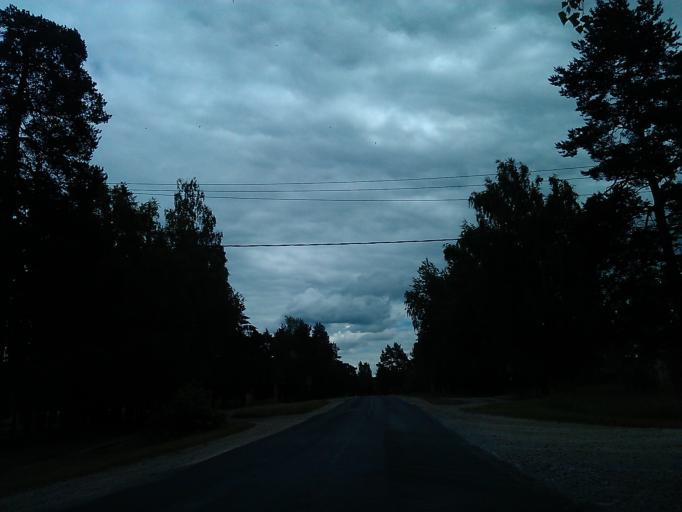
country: LV
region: Dobeles Rajons
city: Dobele
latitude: 56.6490
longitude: 23.2155
